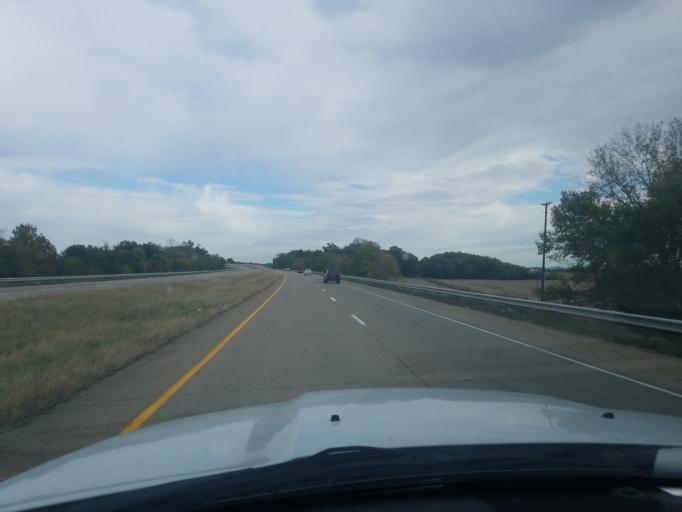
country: US
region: Indiana
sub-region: Vanderburgh County
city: Evansville
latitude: 37.9390
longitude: -87.5031
